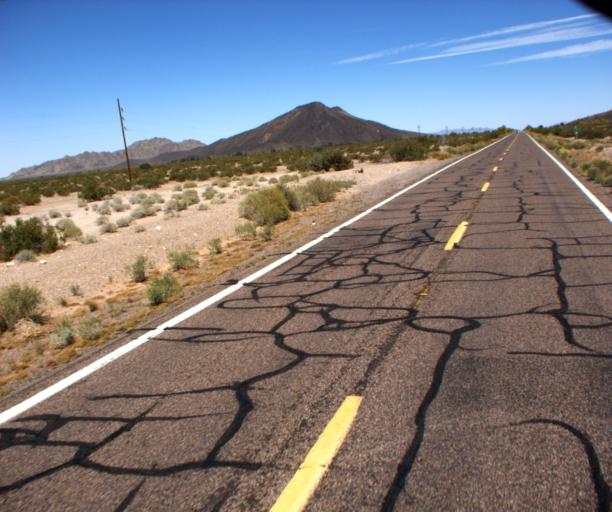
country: US
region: Arizona
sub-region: Maricopa County
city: Gila Bend
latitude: 32.7391
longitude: -112.8315
